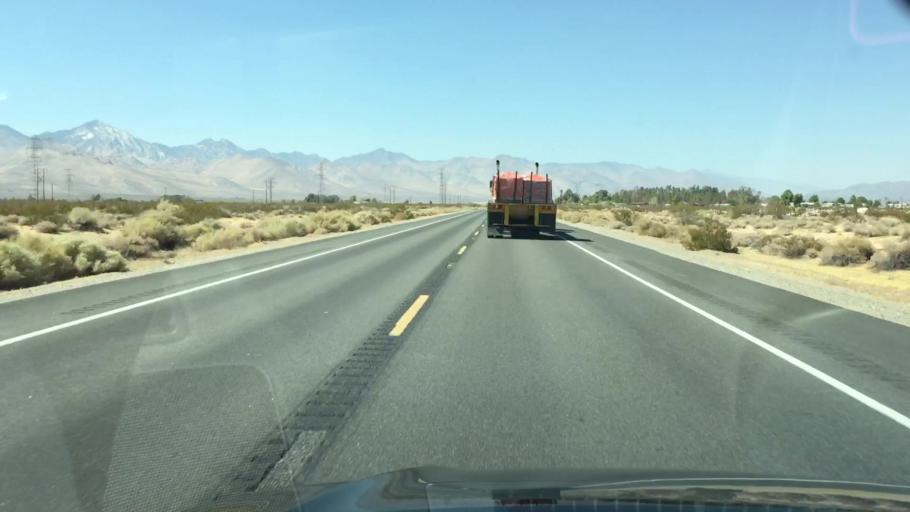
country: US
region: California
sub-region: Kern County
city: China Lake Acres
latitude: 35.6326
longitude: -117.7843
